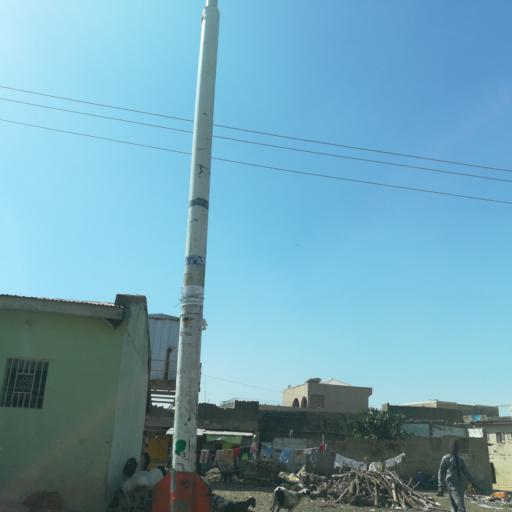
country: NG
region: Kano
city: Kano
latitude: 11.9937
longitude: 8.5312
